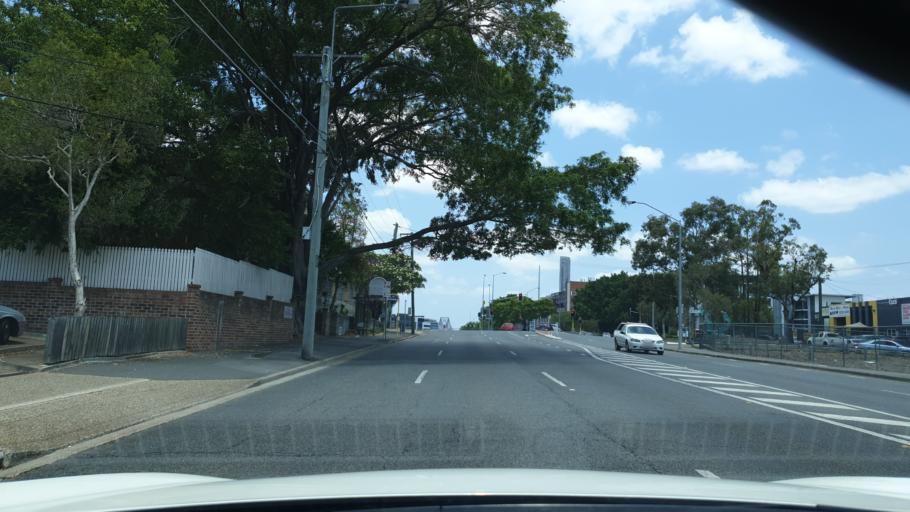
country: AU
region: Queensland
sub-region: Brisbane
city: Fortitude Valley
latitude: -27.4464
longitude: 153.0380
